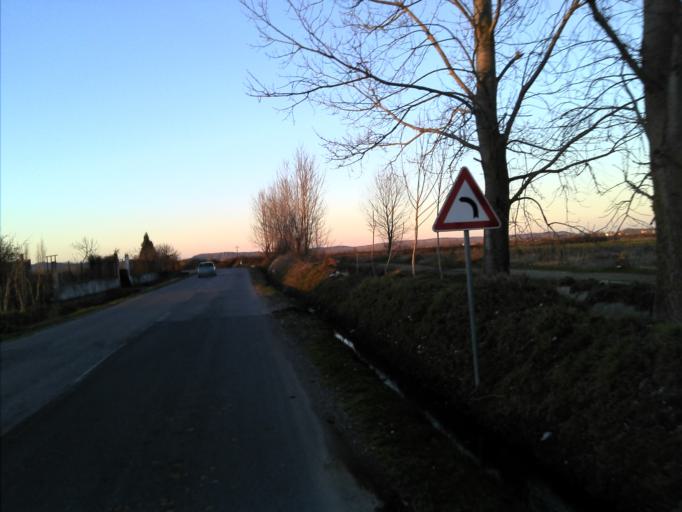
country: AL
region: Shkoder
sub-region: Rrethi i Shkodres
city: Berdica e Madhe
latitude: 42.0074
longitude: 19.4802
